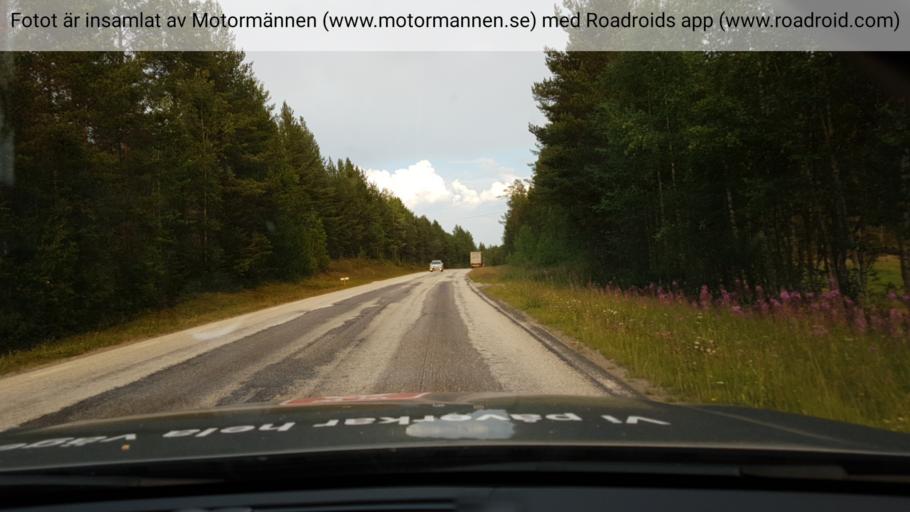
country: SE
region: Jaemtland
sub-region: Harjedalens Kommun
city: Sveg
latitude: 62.4127
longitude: 13.6684
